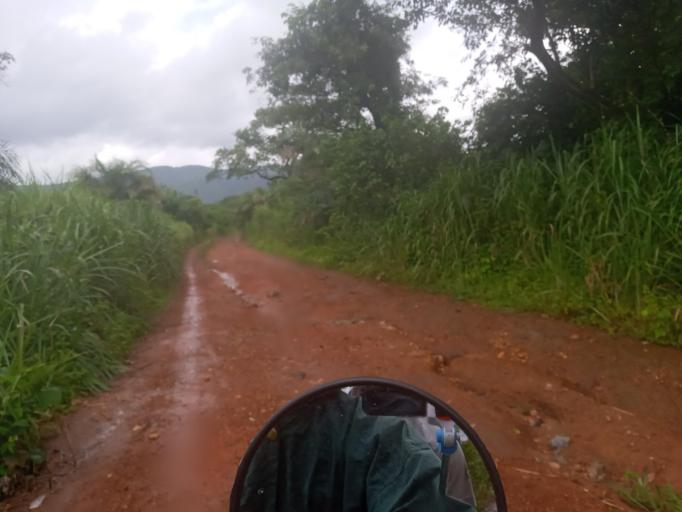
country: SL
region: Northern Province
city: Bumbuna
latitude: 8.9319
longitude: -11.7485
